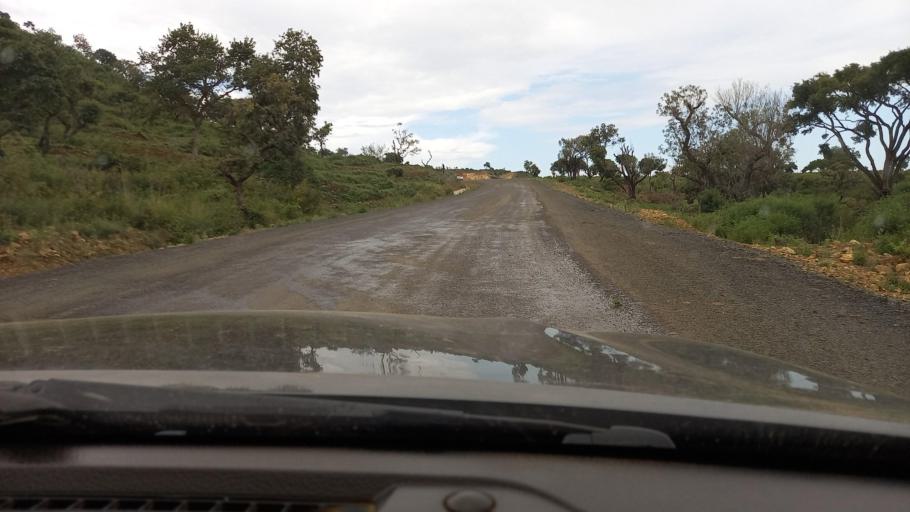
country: ET
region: Southern Nations, Nationalities, and People's Region
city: Mizan Teferi
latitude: 6.2037
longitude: 35.6518
